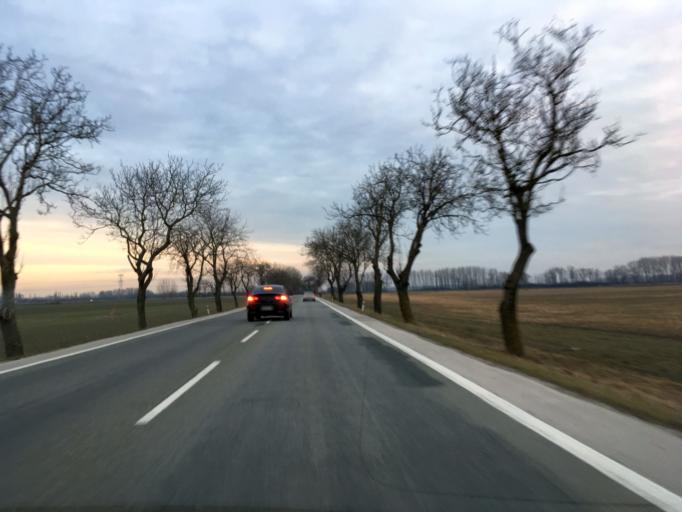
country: SK
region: Trnavsky
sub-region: Okres Dunajska Streda
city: Velky Meder
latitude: 47.8925
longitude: 17.7417
